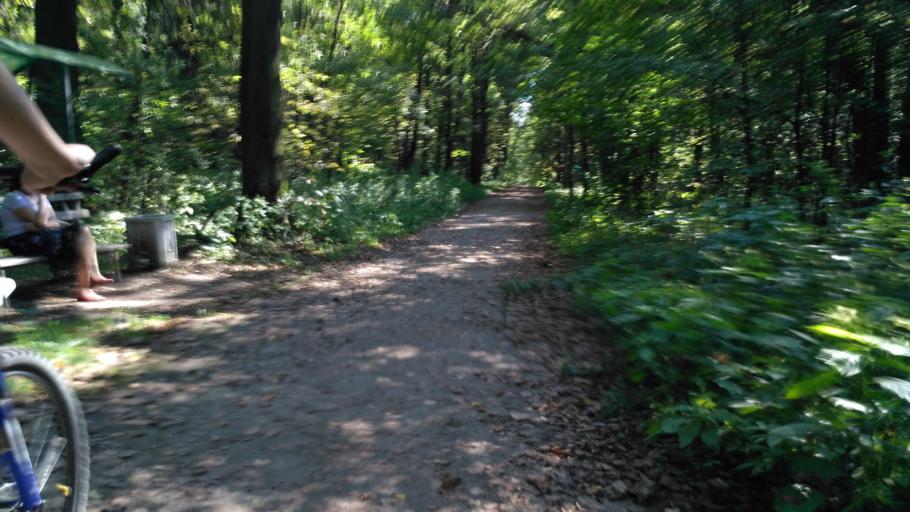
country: RU
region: Moscow
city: Ryazanskiy
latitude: 55.7722
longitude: 37.7593
